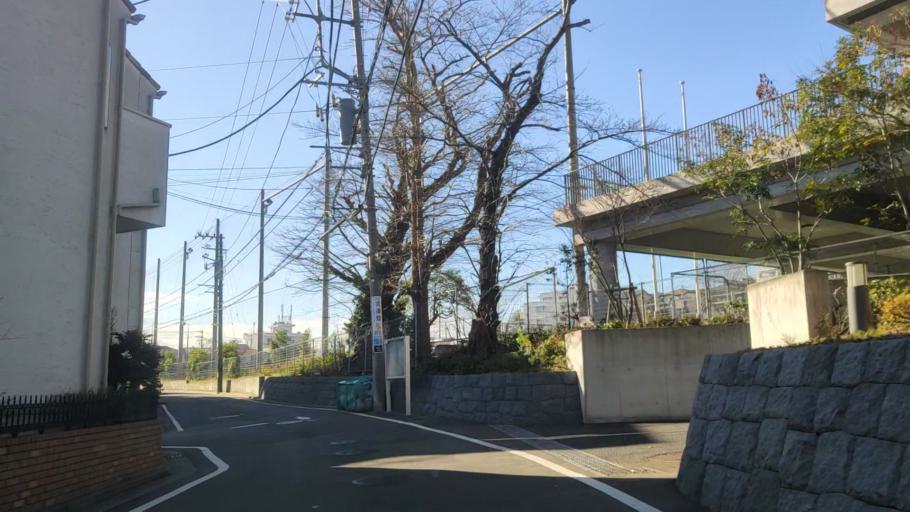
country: JP
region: Kanagawa
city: Yokohama
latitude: 35.4222
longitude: 139.6431
